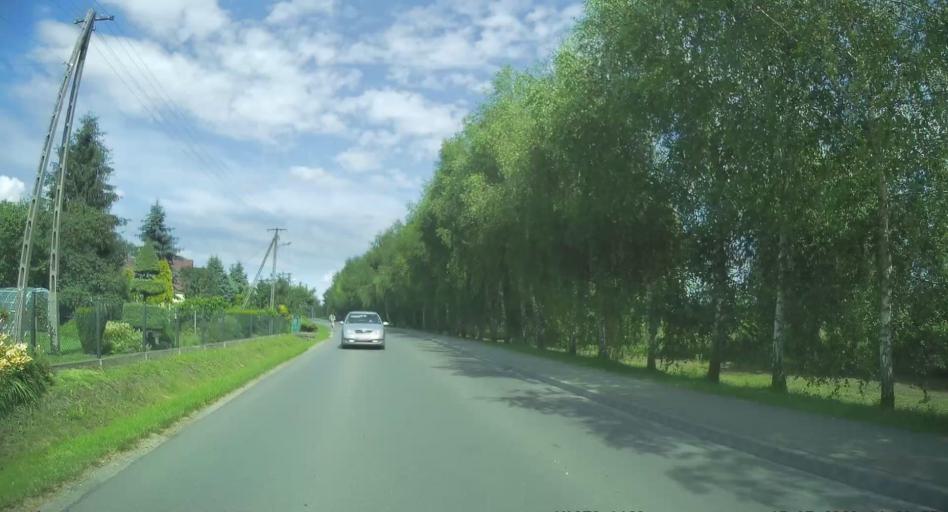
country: PL
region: Subcarpathian Voivodeship
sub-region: Powiat przemyski
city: Zurawica
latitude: 49.8068
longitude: 22.8222
